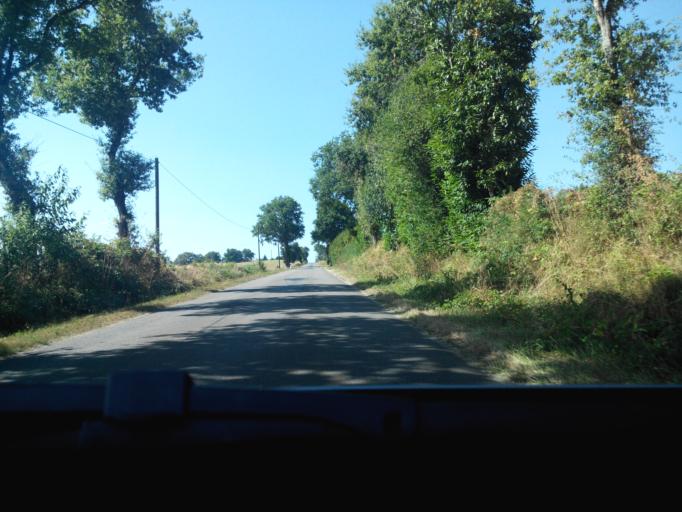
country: FR
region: Poitou-Charentes
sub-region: Departement de la Charente
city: Etagnac
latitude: 45.9366
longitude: 0.7694
